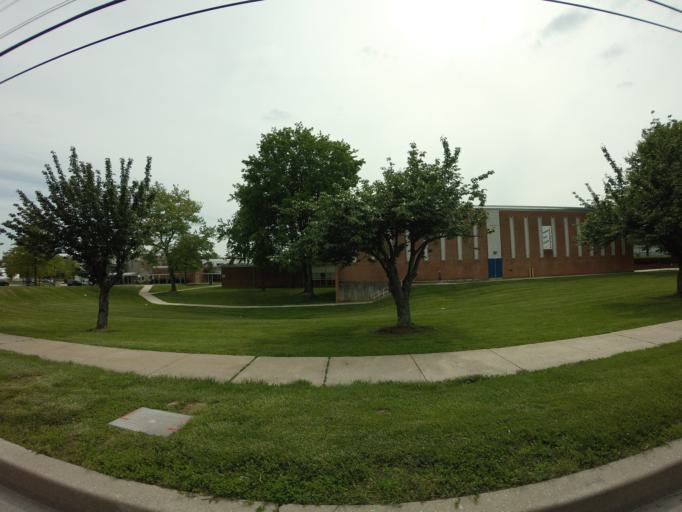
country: US
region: Maryland
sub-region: Baltimore County
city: Reisterstown
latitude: 39.4487
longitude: -76.8163
